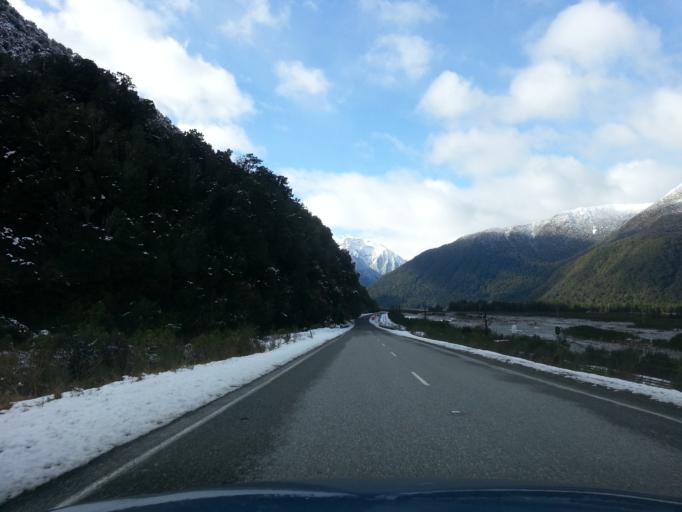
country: NZ
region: West Coast
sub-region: Grey District
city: Greymouth
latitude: -42.7939
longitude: 171.5911
